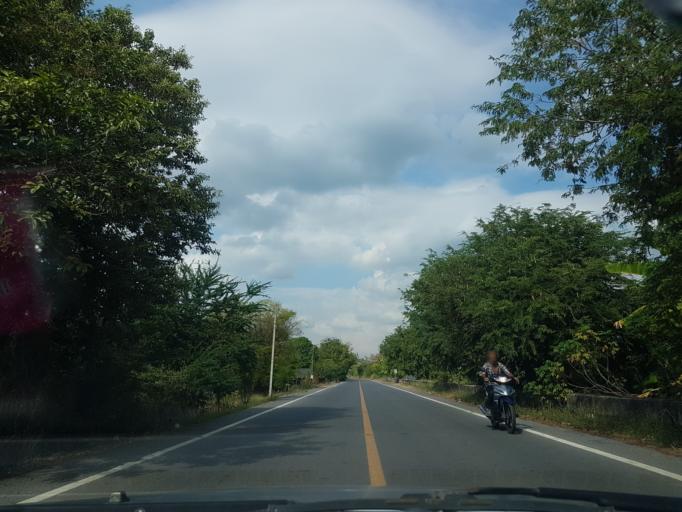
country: TH
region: Pathum Thani
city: Nong Suea
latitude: 14.1481
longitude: 100.8914
